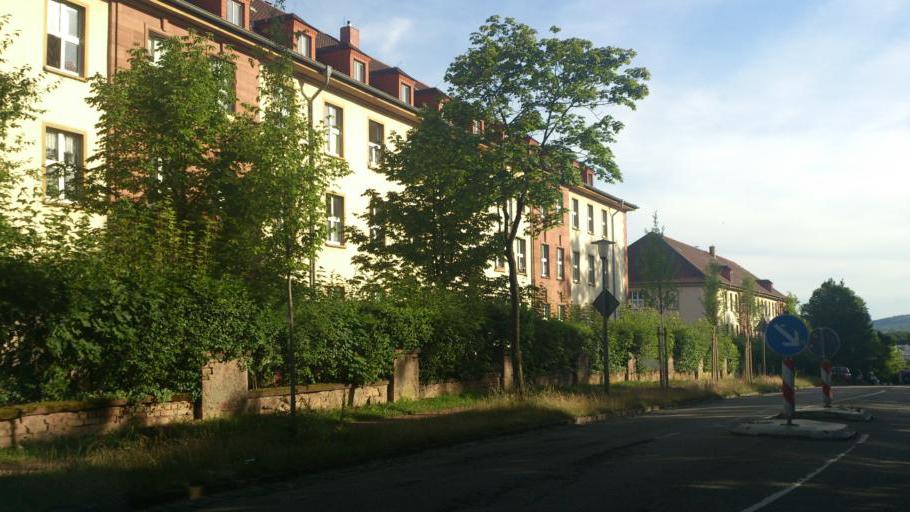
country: DE
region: Saarland
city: Homburg
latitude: 49.3302
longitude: 7.3249
